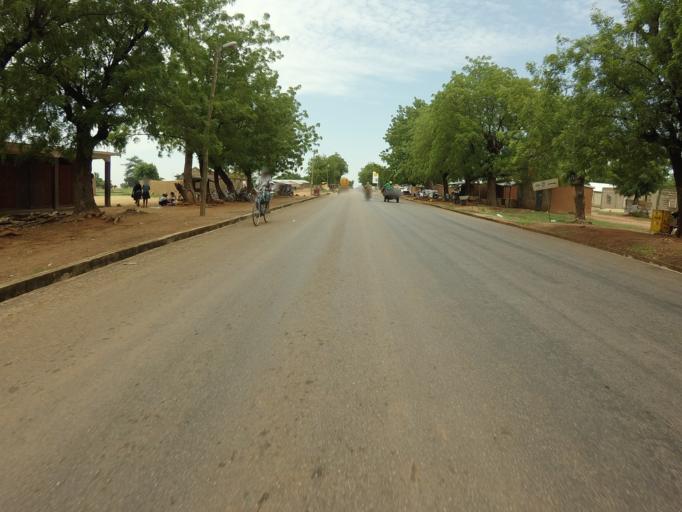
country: GH
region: Upper East
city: Bawku
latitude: 11.0692
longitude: -0.2085
